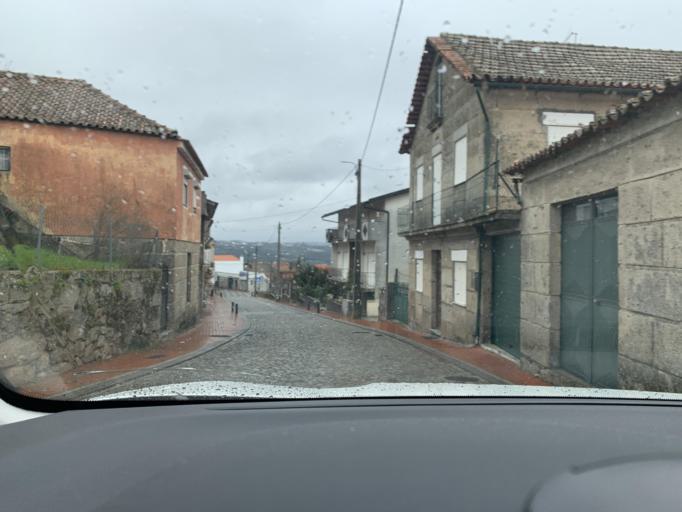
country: PT
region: Viseu
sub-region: Nelas
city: Nelas
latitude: 40.5996
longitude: -7.8439
